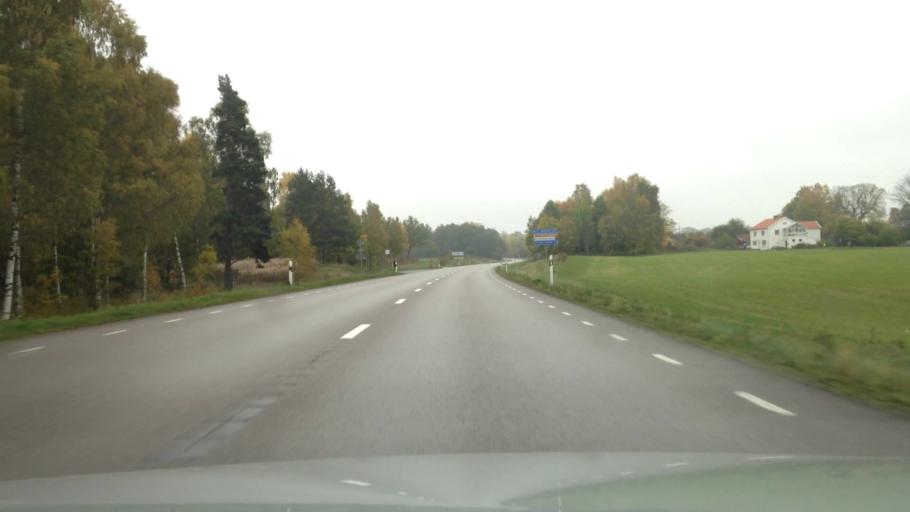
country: SE
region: Vaestra Goetaland
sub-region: Falkopings Kommun
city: Falkoeping
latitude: 58.2511
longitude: 13.5105
